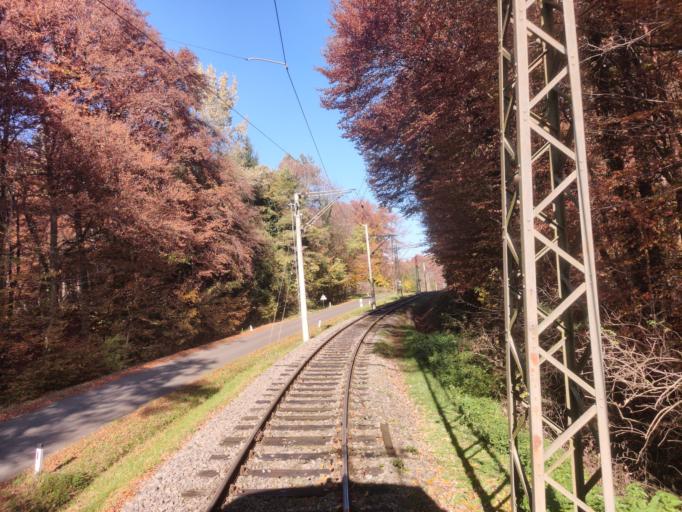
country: AT
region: Styria
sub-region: Politischer Bezirk Suedoststeiermark
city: Gnas
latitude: 46.8823
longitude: 15.8307
